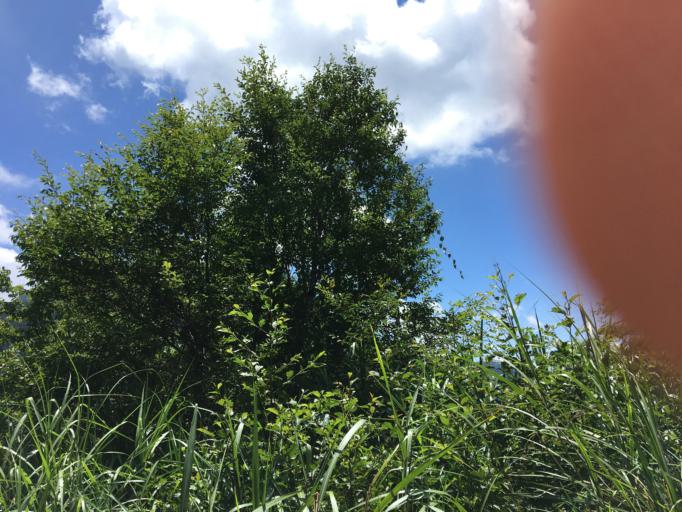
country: TW
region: Taiwan
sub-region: Yilan
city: Yilan
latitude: 24.4916
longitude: 121.5332
